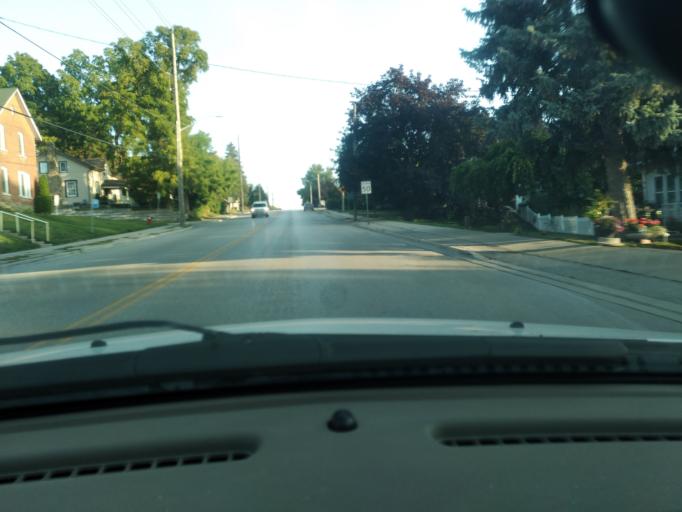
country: CA
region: Ontario
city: Bradford West Gwillimbury
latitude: 44.1180
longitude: -79.5657
